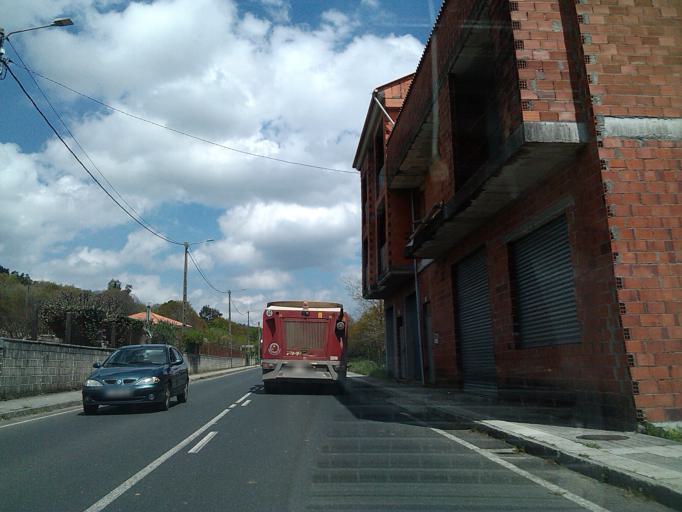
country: ES
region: Galicia
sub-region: Provincia da Coruna
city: Melide
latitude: 42.9675
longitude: -7.9724
